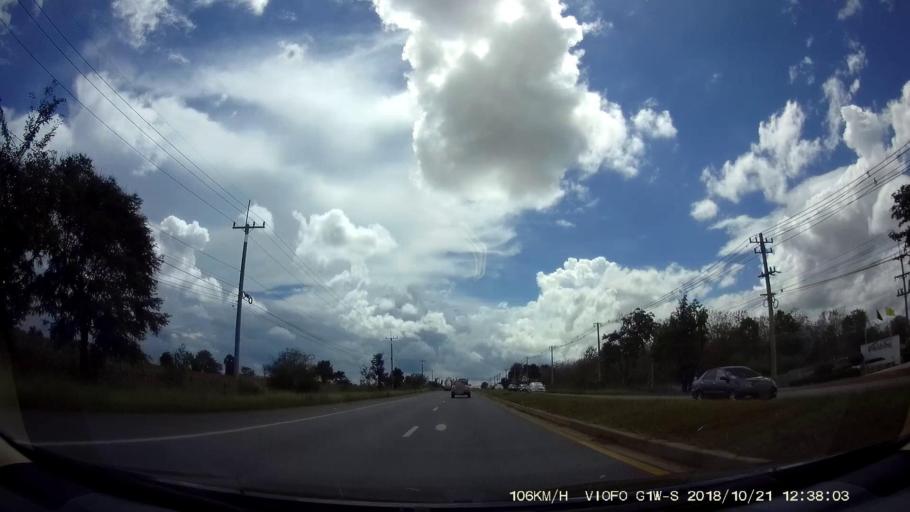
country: TH
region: Nakhon Ratchasima
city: Amphoe Sikhiu
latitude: 15.0596
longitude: 101.7080
